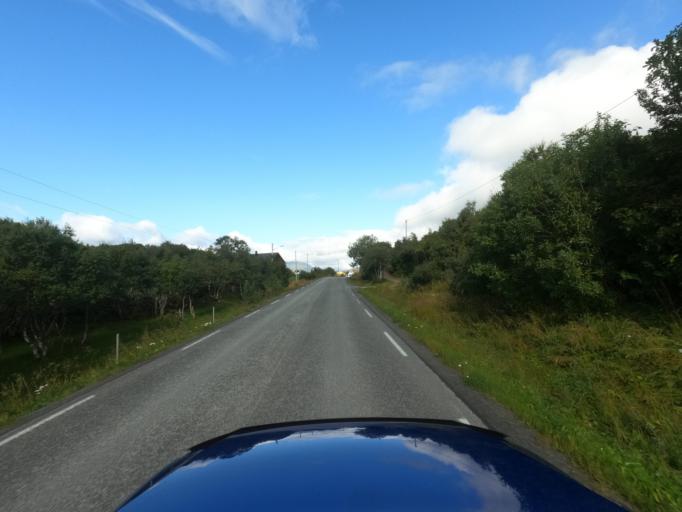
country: NO
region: Nordland
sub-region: Vestvagoy
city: Leknes
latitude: 68.1264
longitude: 13.6378
